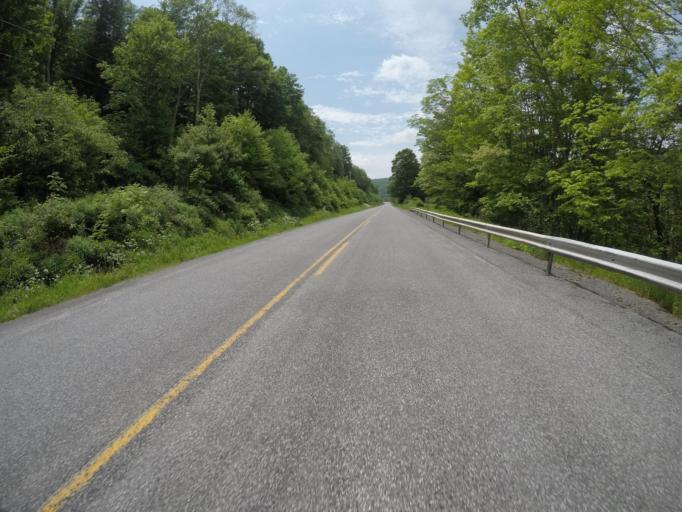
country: US
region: New York
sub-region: Delaware County
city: Stamford
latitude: 42.1720
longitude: -74.6768
